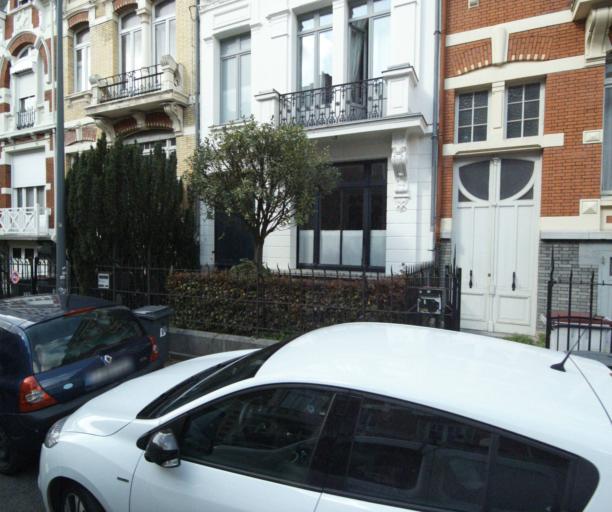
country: FR
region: Nord-Pas-de-Calais
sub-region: Departement du Nord
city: La Madeleine
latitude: 50.6418
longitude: 3.0890
